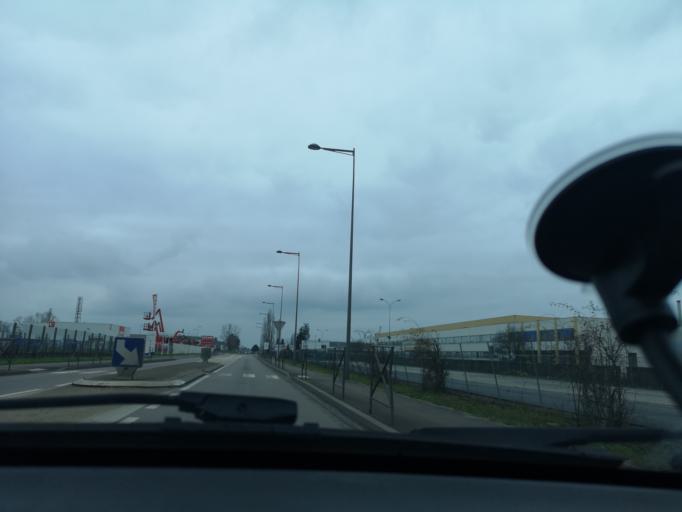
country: FR
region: Bourgogne
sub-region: Departement de Saone-et-Loire
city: Virey-le-Grand
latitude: 46.8182
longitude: 4.8607
